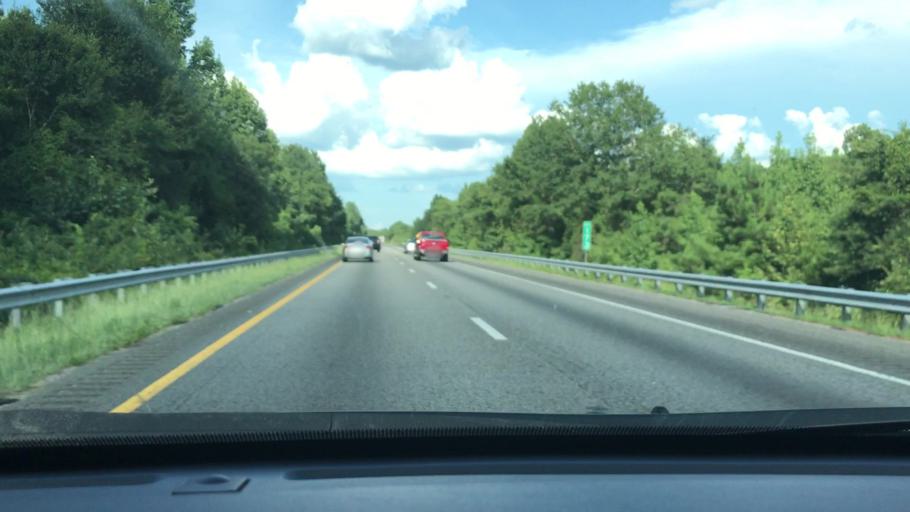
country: US
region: South Carolina
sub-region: Florence County
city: Florence
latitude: 34.2864
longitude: -79.6654
